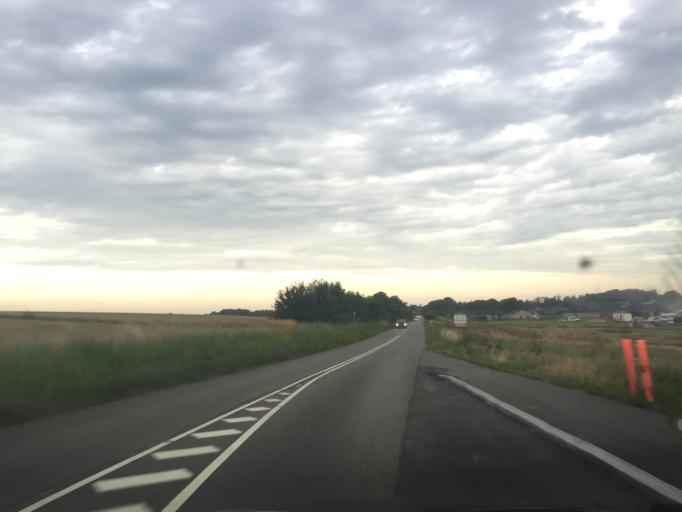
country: DK
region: Zealand
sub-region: Roskilde Kommune
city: Gundsomagle
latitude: 55.7331
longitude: 12.1689
